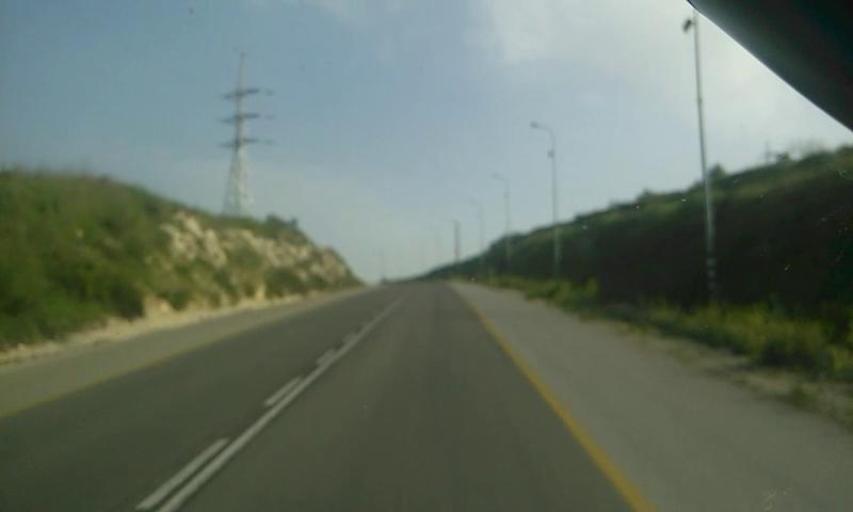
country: PS
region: West Bank
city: Sarrah
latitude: 32.1983
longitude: 35.1853
